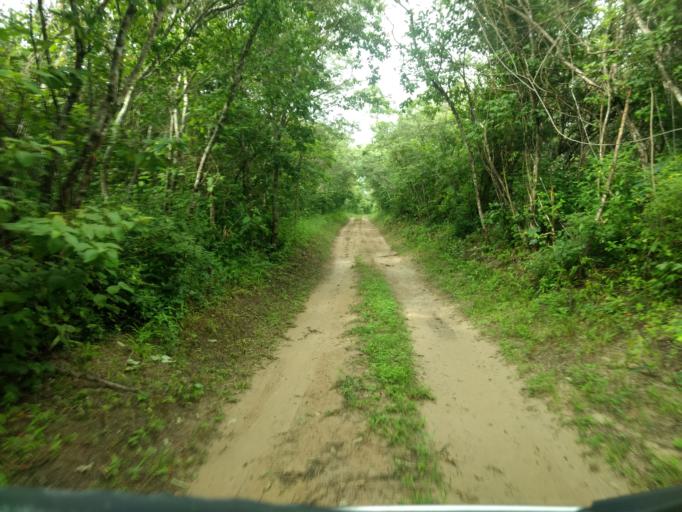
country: BR
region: Ceara
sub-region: Crateus
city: Crateus
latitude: -5.1534
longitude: -40.9200
